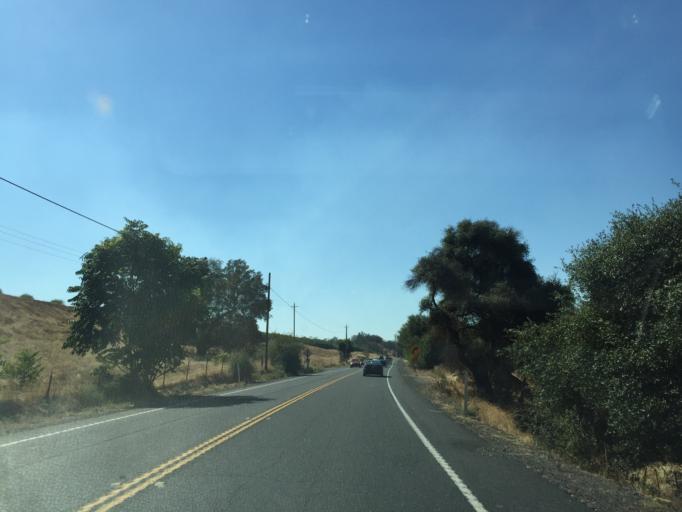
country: US
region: California
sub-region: Stanislaus County
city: East Oakdale
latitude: 37.7913
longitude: -120.7261
